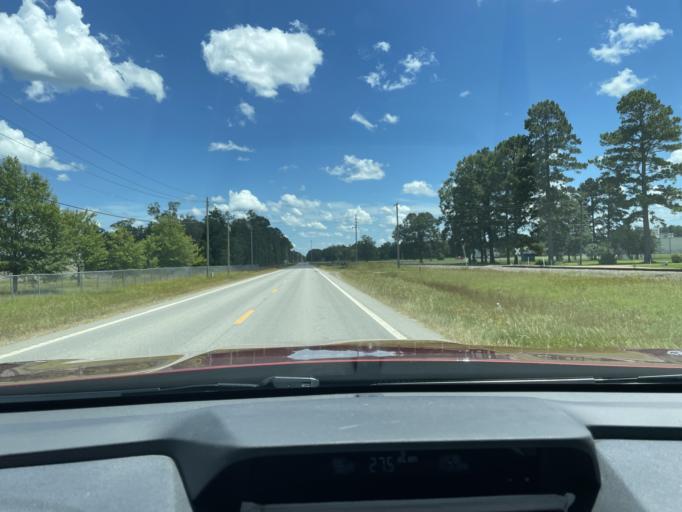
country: US
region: Arkansas
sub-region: Drew County
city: Monticello
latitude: 33.6181
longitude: -91.7467
